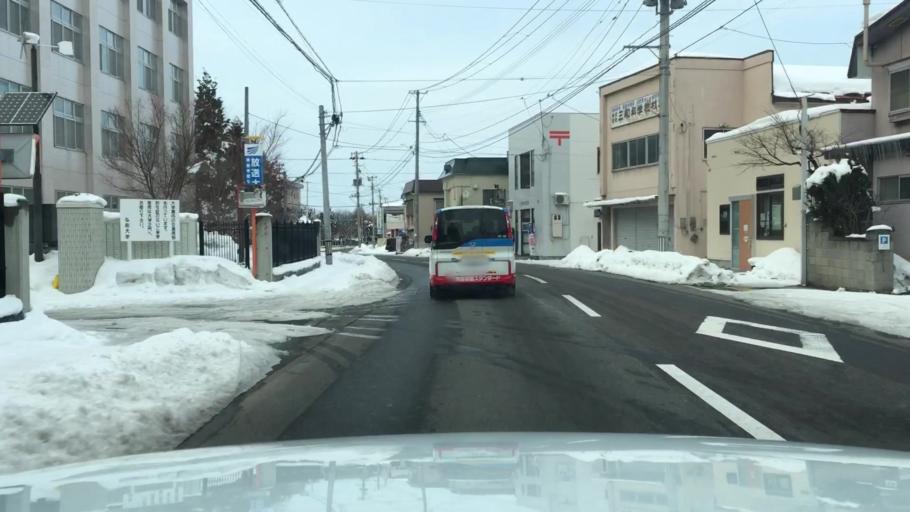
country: JP
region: Aomori
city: Hirosaki
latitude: 40.5875
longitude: 140.4747
